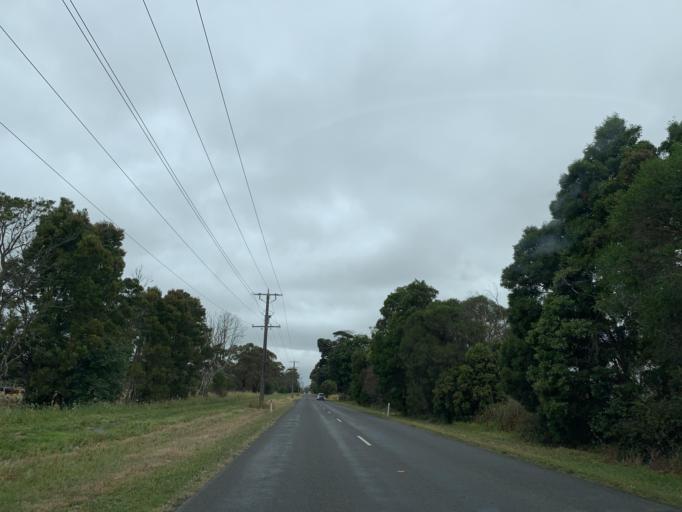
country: AU
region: Victoria
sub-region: Cardinia
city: Pakenham South
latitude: -38.1695
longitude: 145.5518
